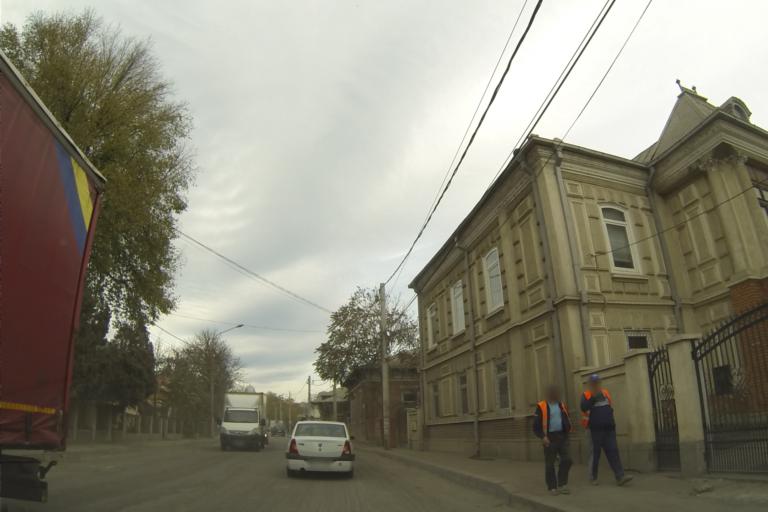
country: RO
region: Olt
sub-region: Municipiul Slatina
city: Slatina
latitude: 44.4285
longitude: 24.3542
